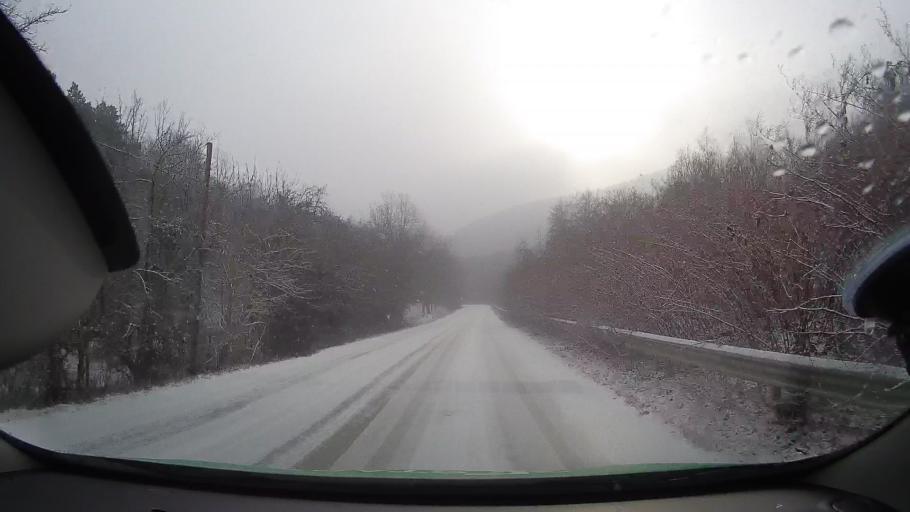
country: RO
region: Alba
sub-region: Comuna Livezile
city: Livezile
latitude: 46.3539
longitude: 23.6181
